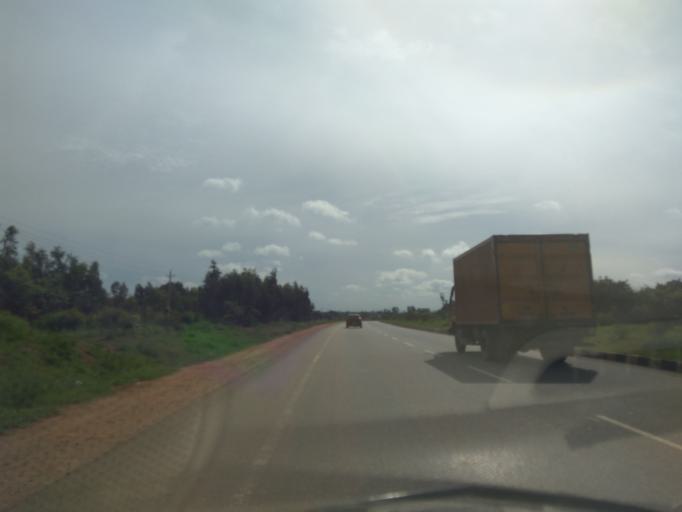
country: IN
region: Karnataka
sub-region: Bangalore Rural
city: Dasarahalli
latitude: 13.0966
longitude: 77.8521
